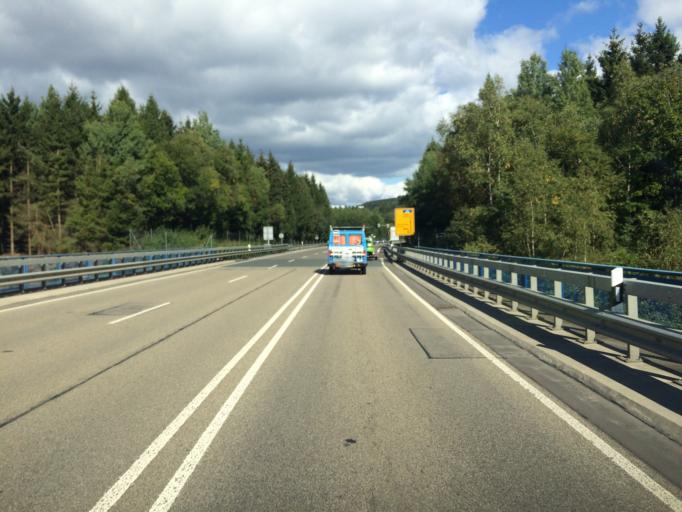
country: DE
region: Hesse
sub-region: Regierungsbezirk Giessen
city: Haiger
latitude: 50.7583
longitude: 8.1479
